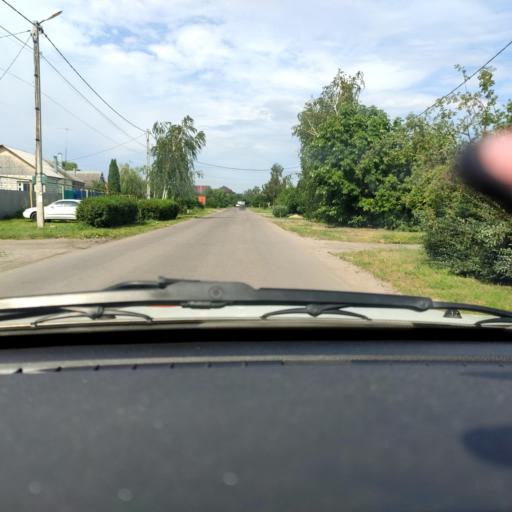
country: RU
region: Voronezj
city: Novaya Usman'
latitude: 51.6278
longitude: 39.4077
